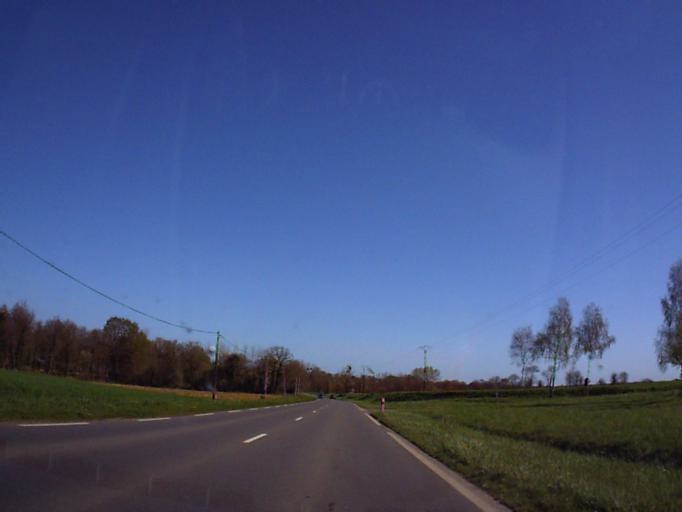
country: FR
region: Brittany
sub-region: Departement d'Ille-et-Vilaine
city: Quedillac
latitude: 48.2393
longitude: -2.1699
